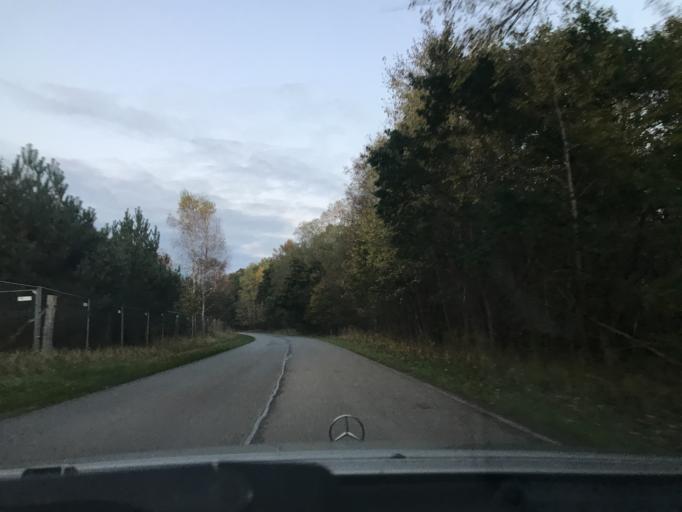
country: DE
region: Mecklenburg-Vorpommern
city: Kroslin
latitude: 54.1493
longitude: 13.7907
